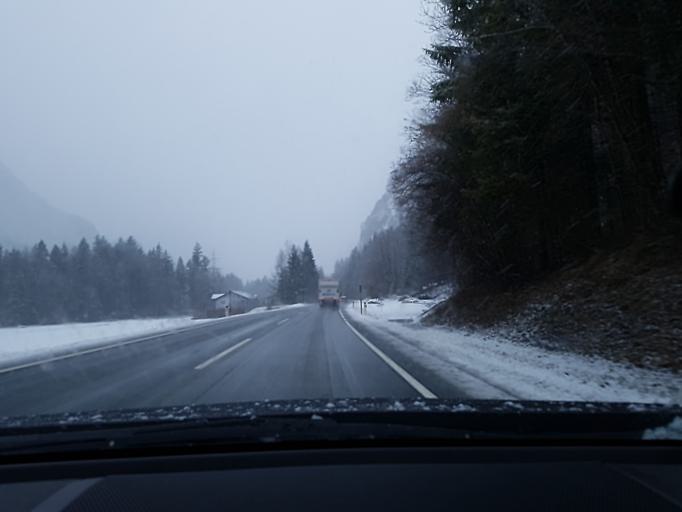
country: AT
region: Salzburg
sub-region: Politischer Bezirk Hallein
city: Scheffau am Tennengebirge
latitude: 47.5801
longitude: 13.2531
